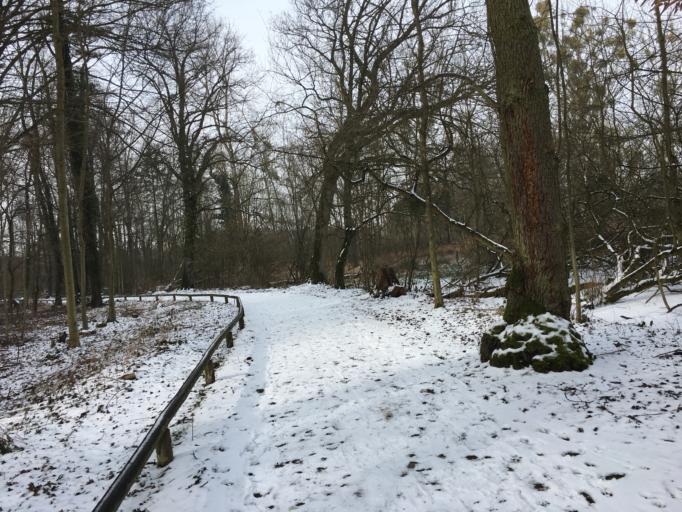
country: DE
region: North Rhine-Westphalia
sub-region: Regierungsbezirk Koln
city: Dueren
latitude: 50.7770
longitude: 6.4969
